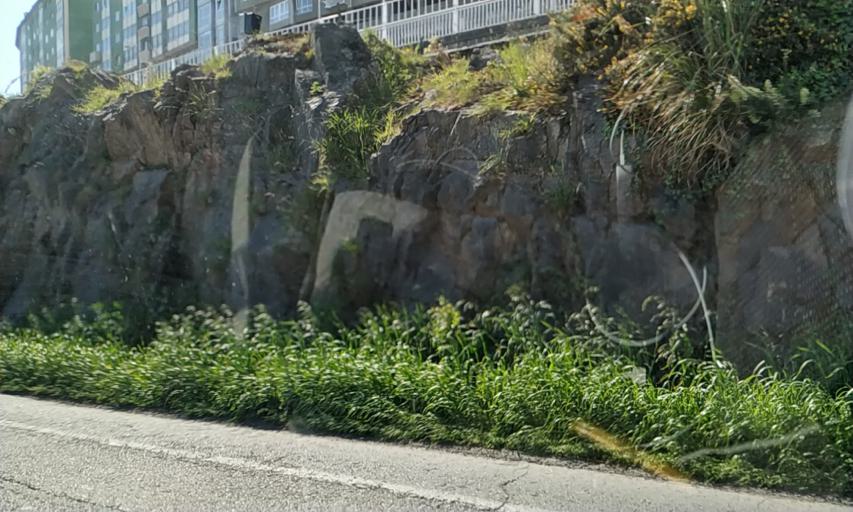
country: ES
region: Galicia
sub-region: Provincia da Coruna
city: A Coruna
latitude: 43.3527
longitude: -8.3871
